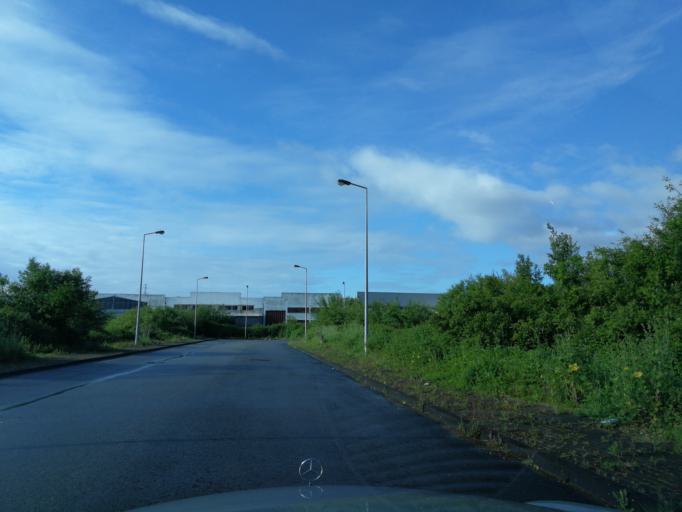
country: PT
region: Braga
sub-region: Braga
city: Braga
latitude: 41.5673
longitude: -8.4486
